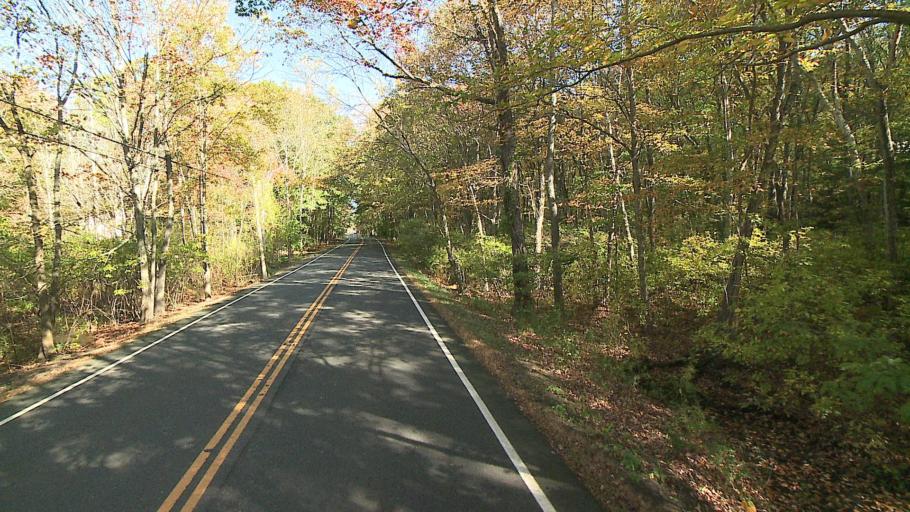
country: US
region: Connecticut
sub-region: Fairfield County
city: Trumbull
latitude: 41.2662
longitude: -73.2987
